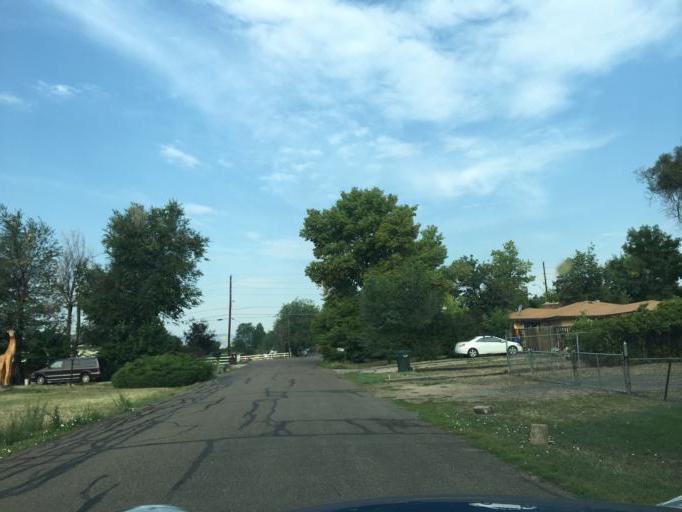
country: US
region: Colorado
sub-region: Jefferson County
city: Wheat Ridge
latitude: 39.7438
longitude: -105.1083
